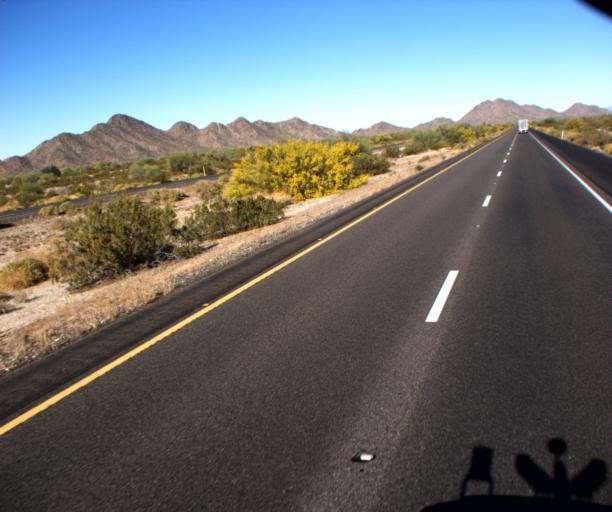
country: US
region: Arizona
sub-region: Maricopa County
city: Gila Bend
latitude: 32.8971
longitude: -112.5034
